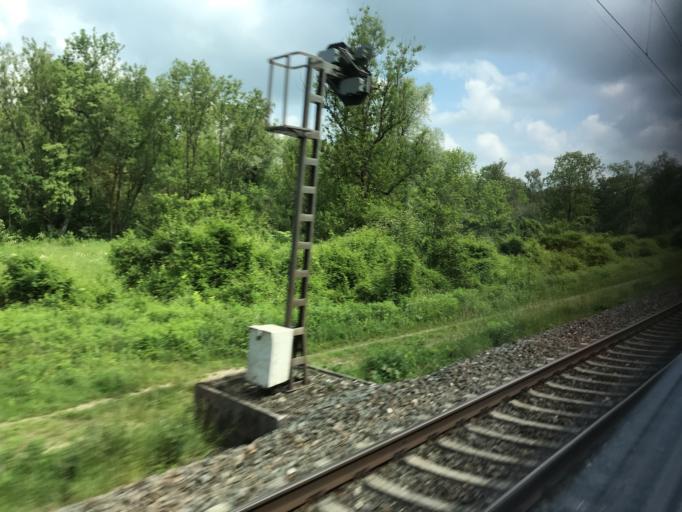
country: DE
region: Bavaria
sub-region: Swabia
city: Leipheim
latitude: 48.4412
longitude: 10.1958
